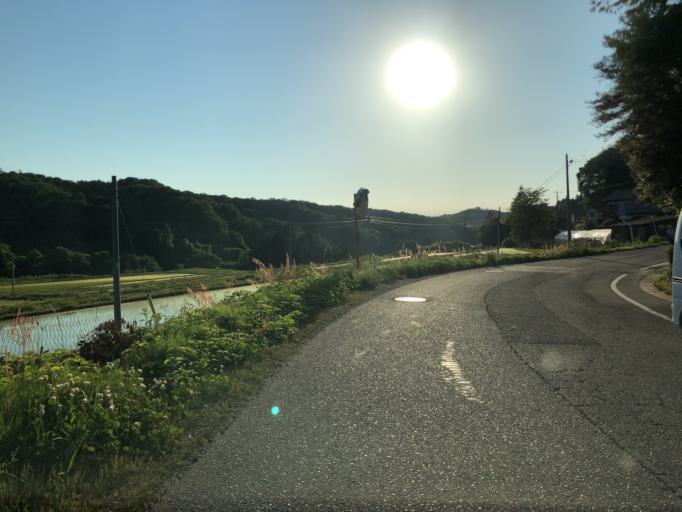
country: JP
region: Fukushima
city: Ishikawa
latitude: 37.0442
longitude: 140.4333
